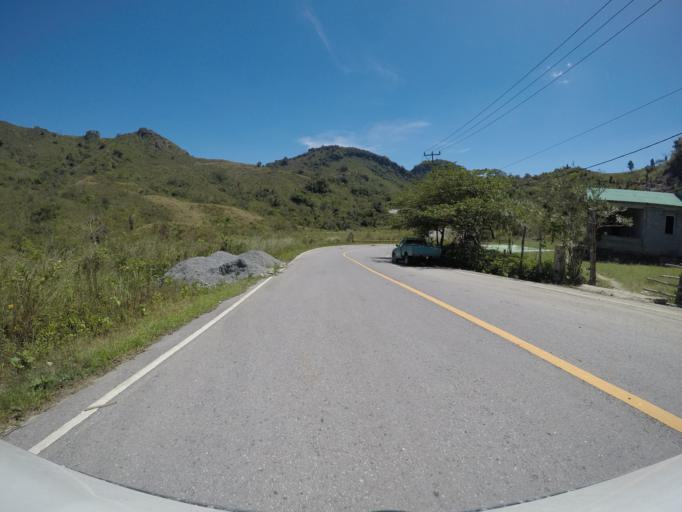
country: TL
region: Manatuto
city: Manatuto
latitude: -8.7625
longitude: 125.9691
